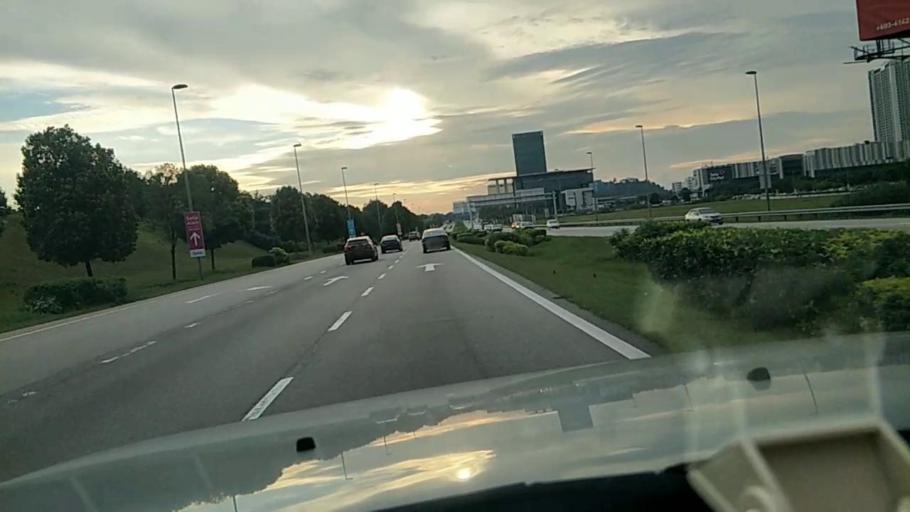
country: MY
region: Selangor
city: Shah Alam
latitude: 3.1049
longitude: 101.4666
